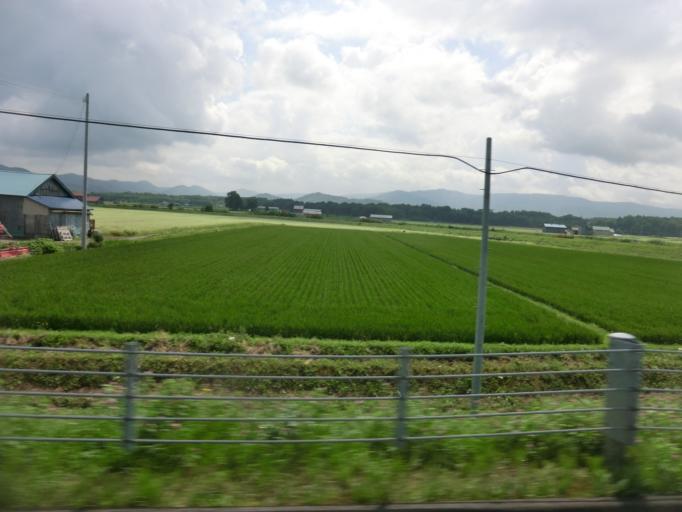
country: JP
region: Hokkaido
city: Fukagawa
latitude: 43.9936
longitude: 142.1395
